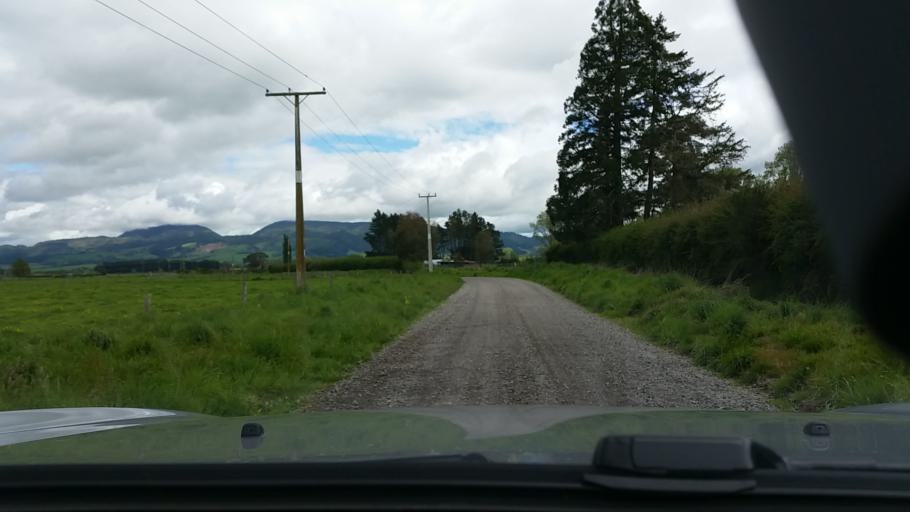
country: NZ
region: Bay of Plenty
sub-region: Rotorua District
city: Rotorua
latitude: -38.4068
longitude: 176.3733
